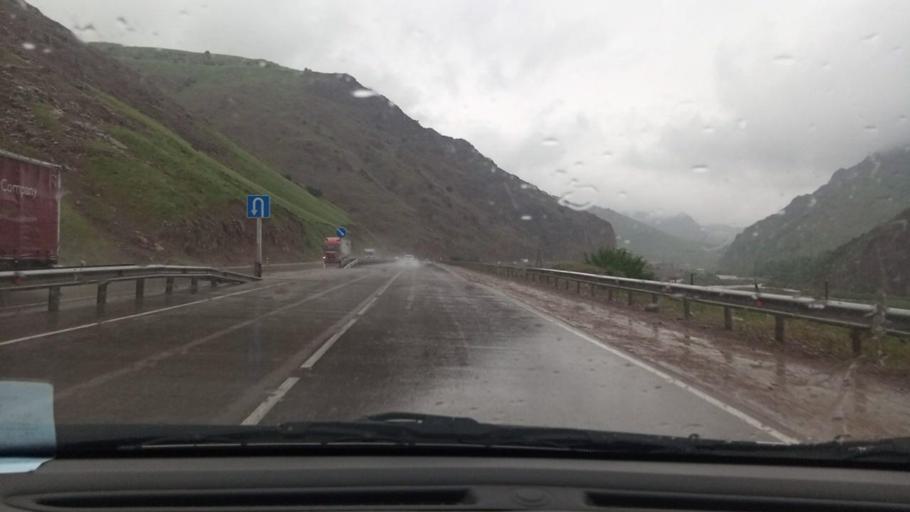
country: UZ
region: Toshkent
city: Angren
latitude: 41.1112
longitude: 70.3378
